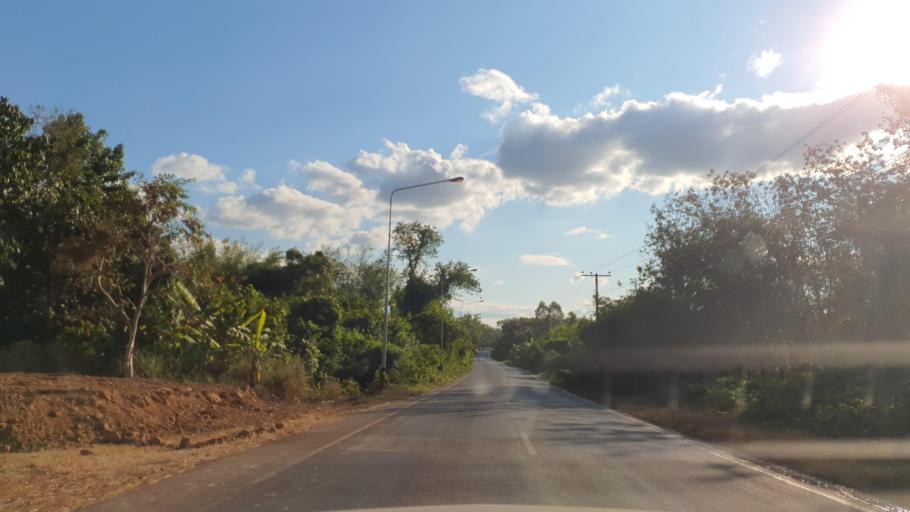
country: TH
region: Changwat Bueng Kan
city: Si Wilai
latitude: 18.1463
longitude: 103.8973
